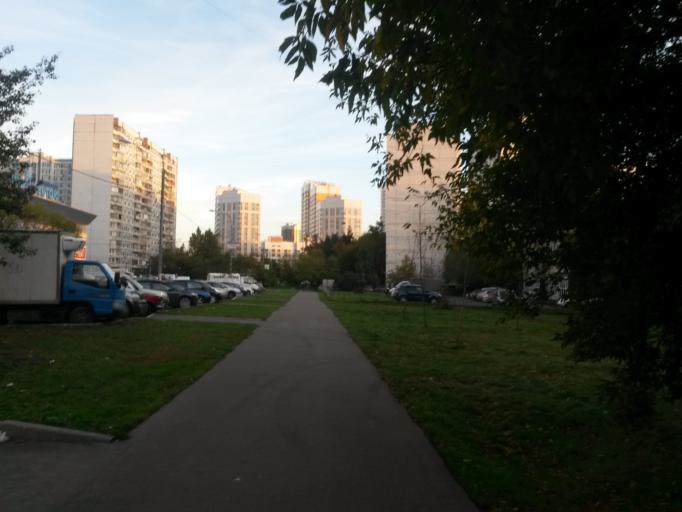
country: RU
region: Moscow
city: Zagor'ye
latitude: 55.5831
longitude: 37.6694
